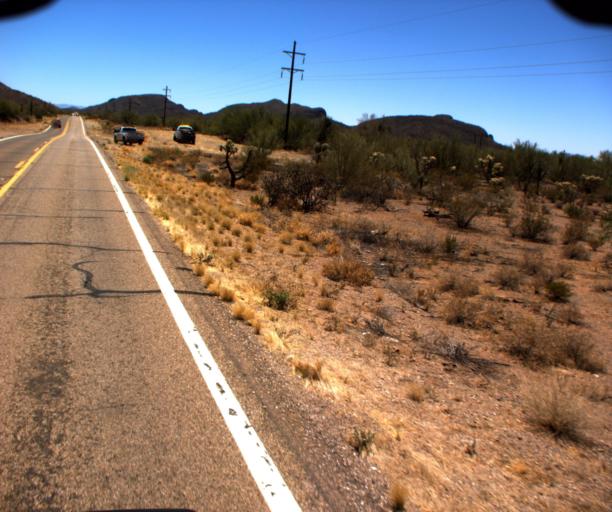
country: US
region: Arizona
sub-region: Pima County
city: Sells
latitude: 31.9808
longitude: -111.9694
